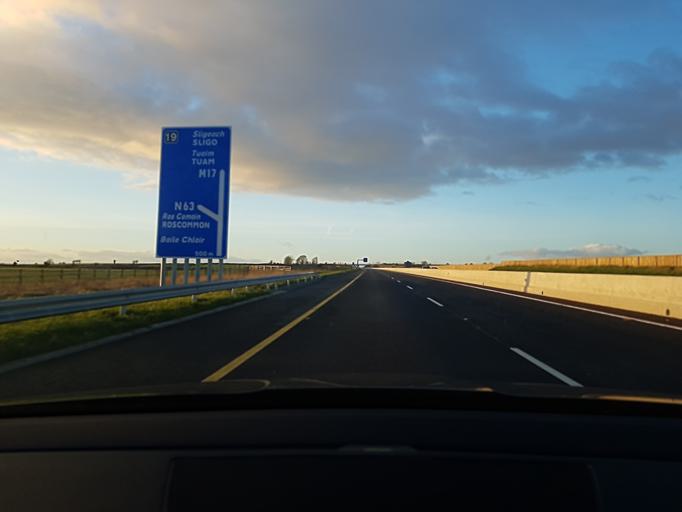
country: IE
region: Connaught
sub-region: County Galway
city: Athenry
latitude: 53.3962
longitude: -8.8071
